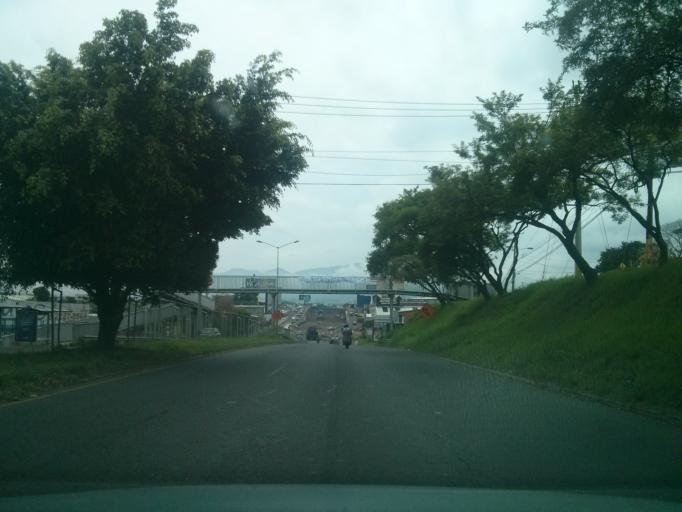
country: CR
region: San Jose
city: Alajuelita
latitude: 9.9107
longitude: -84.0827
